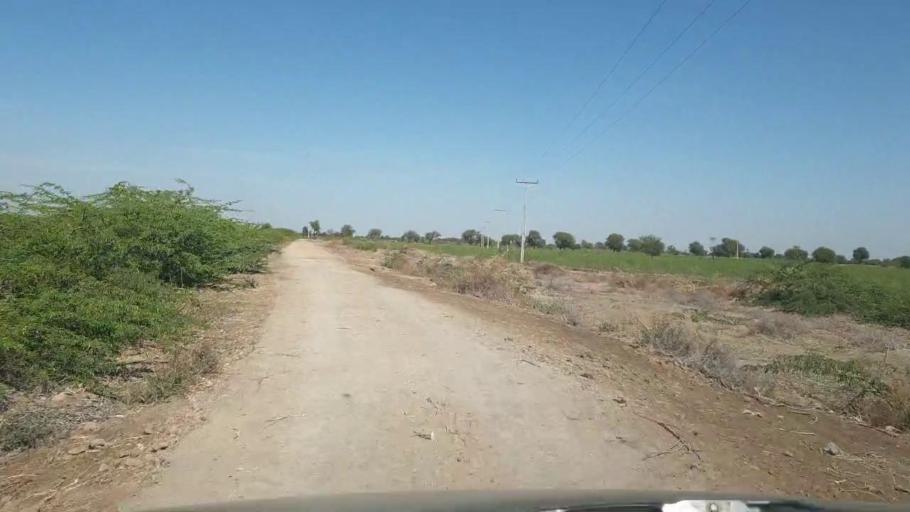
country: PK
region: Sindh
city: Dhoro Naro
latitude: 25.4212
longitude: 69.6194
